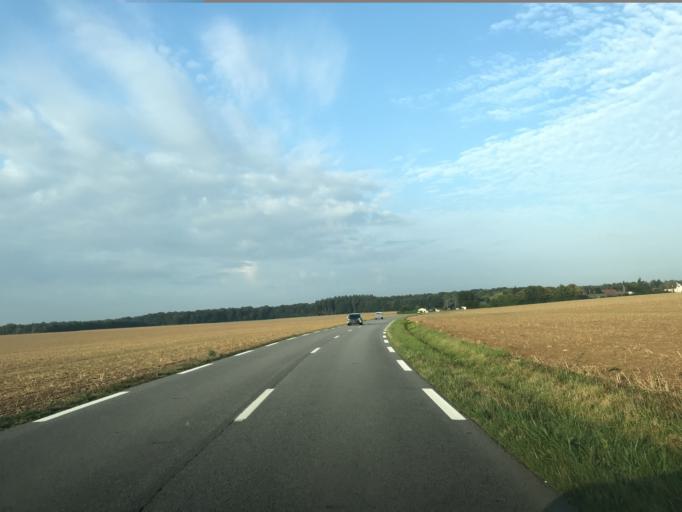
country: FR
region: Haute-Normandie
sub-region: Departement de l'Eure
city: Gravigny
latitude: 49.0668
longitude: 1.2090
